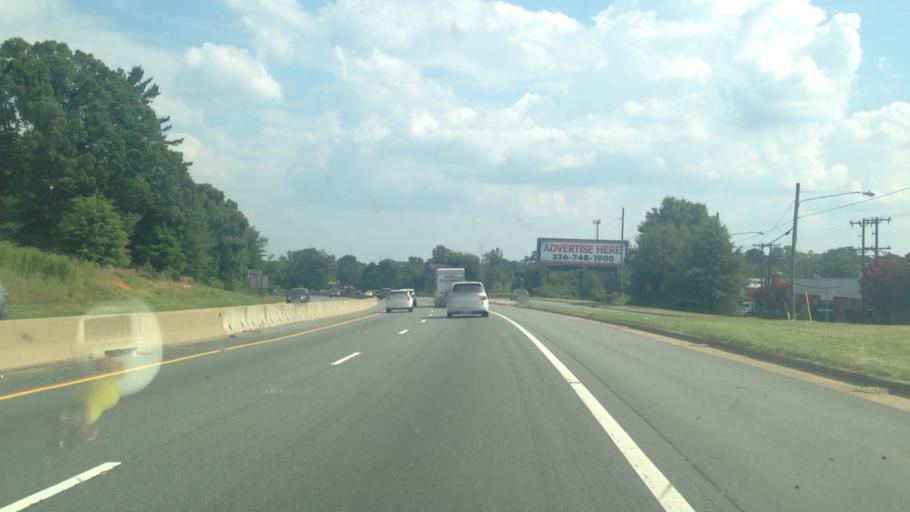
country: US
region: North Carolina
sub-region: Forsyth County
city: Winston-Salem
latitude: 36.1368
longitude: -80.2395
